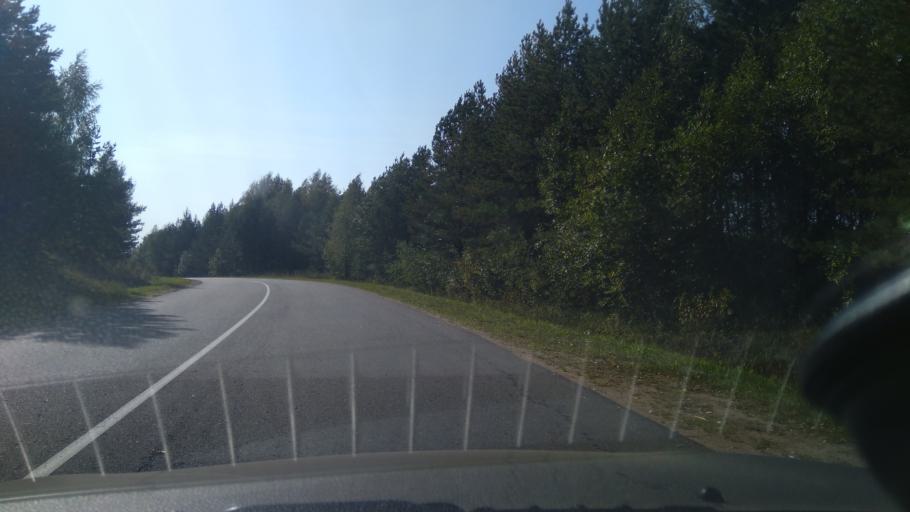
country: BY
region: Minsk
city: Rakaw
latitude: 54.0183
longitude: 27.0502
